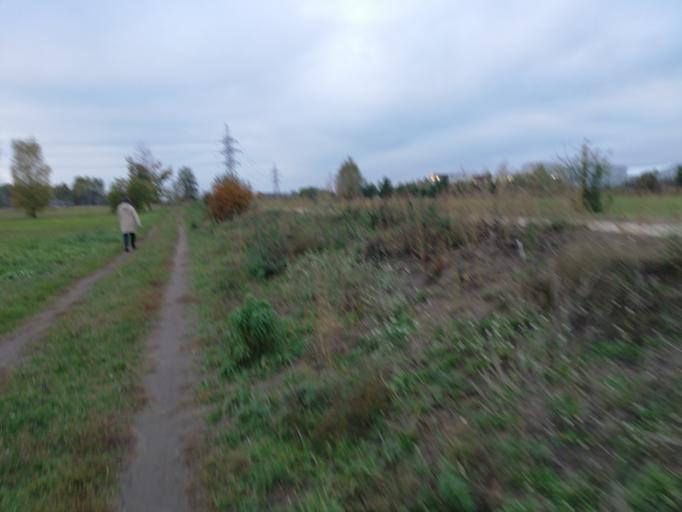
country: LV
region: Stopini
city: Ulbroka
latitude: 56.9484
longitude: 24.2327
